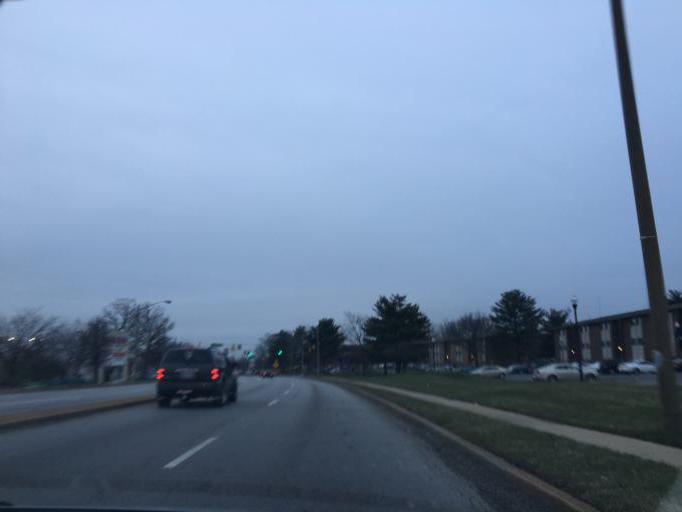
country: US
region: Maryland
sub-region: Baltimore County
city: Woodlawn
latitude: 39.3118
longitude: -76.7548
